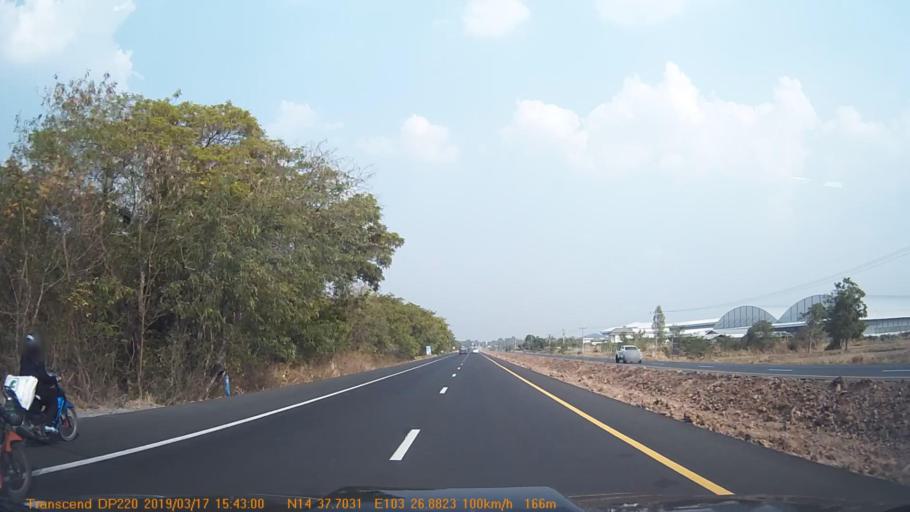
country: TH
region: Surin
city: Prasat
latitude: 14.6282
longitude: 103.4485
